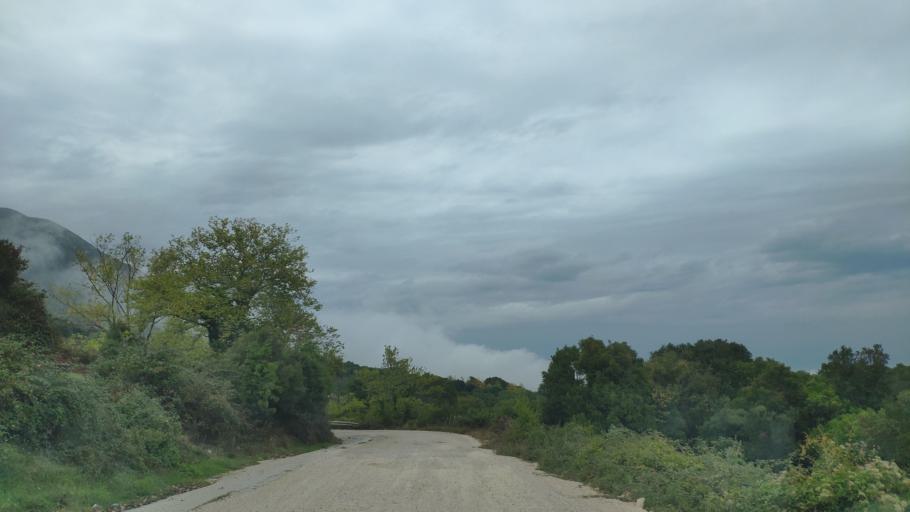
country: GR
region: Epirus
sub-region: Nomos Thesprotias
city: Paramythia
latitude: 39.4592
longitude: 20.6785
